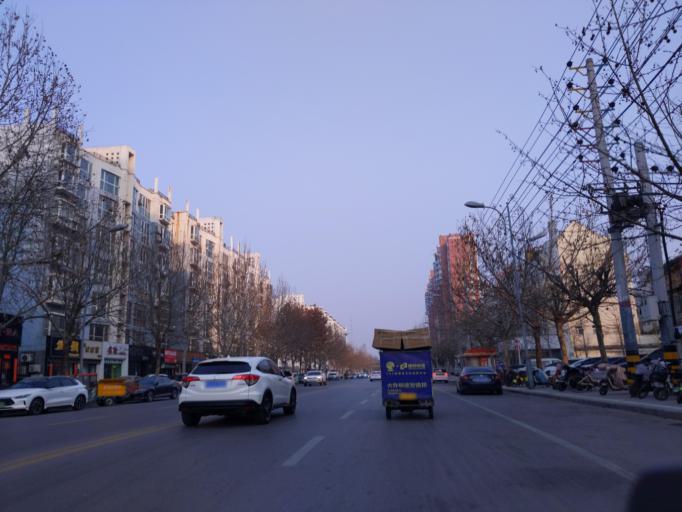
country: CN
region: Henan Sheng
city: Zhongyuanlu
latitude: 35.7742
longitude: 115.0618
